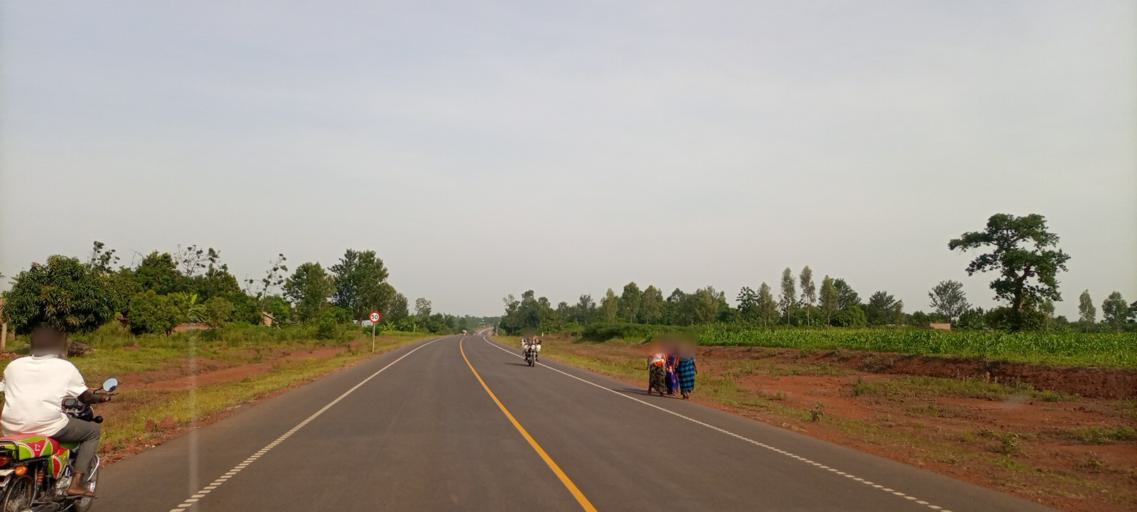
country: UG
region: Eastern Region
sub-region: Budaka District
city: Budaka
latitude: 1.1014
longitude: 33.9978
